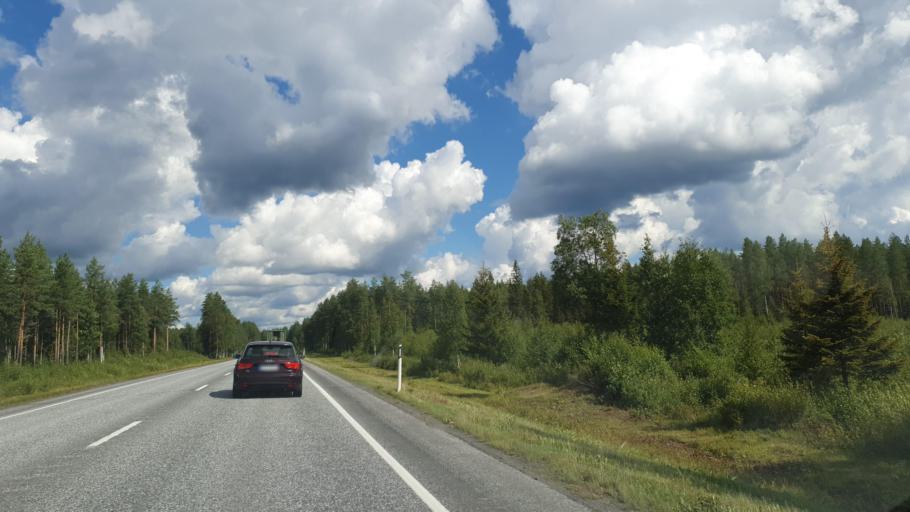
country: FI
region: Kainuu
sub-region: Kajaani
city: Kajaani
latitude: 64.1329
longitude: 27.4842
